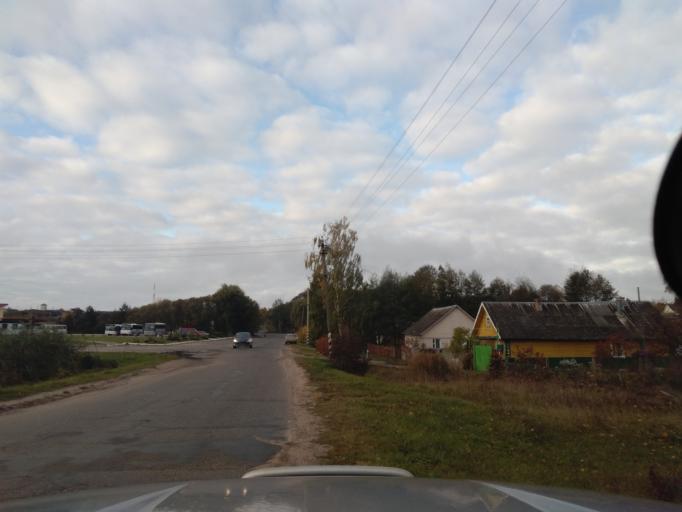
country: BY
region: Minsk
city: Kapyl'
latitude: 53.1592
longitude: 27.0916
